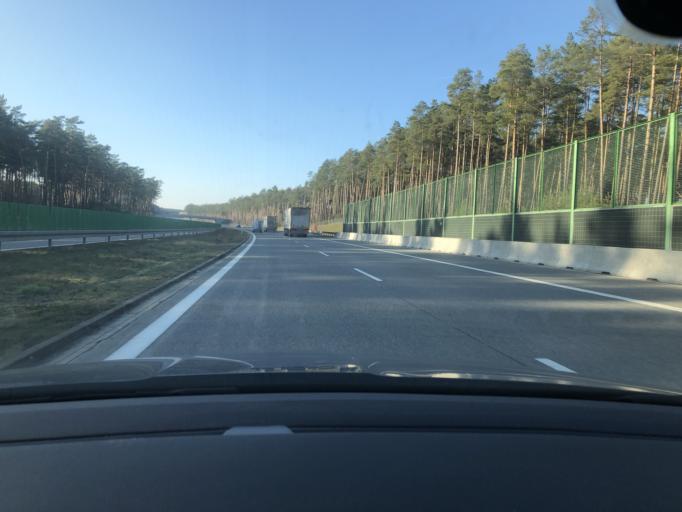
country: PL
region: Lubusz
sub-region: Powiat swiebodzinski
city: Lagow
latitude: 52.3093
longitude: 15.2428
